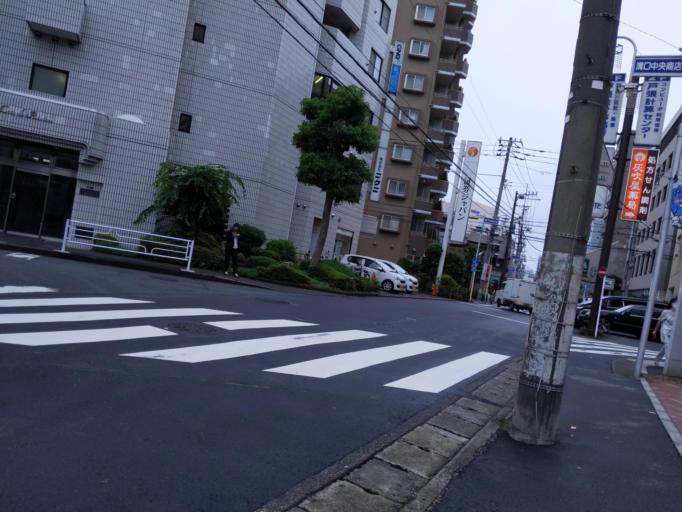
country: JP
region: Tokyo
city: Chofugaoka
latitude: 35.6018
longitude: 139.6168
